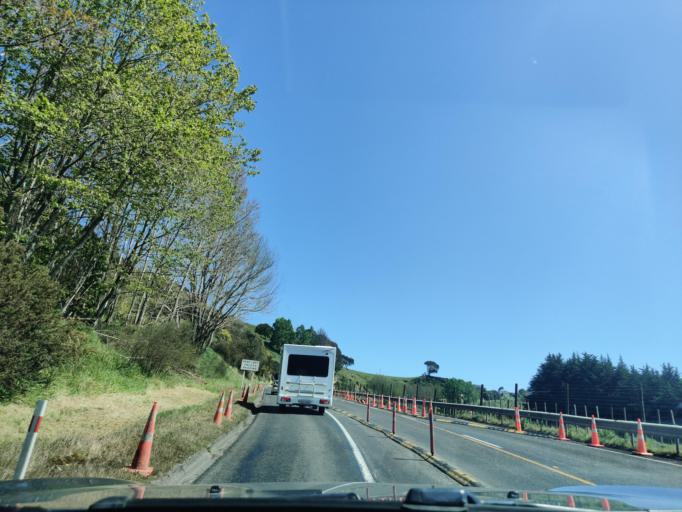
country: NZ
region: Manawatu-Wanganui
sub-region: Wanganui District
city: Wanganui
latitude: -39.8428
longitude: 174.9232
